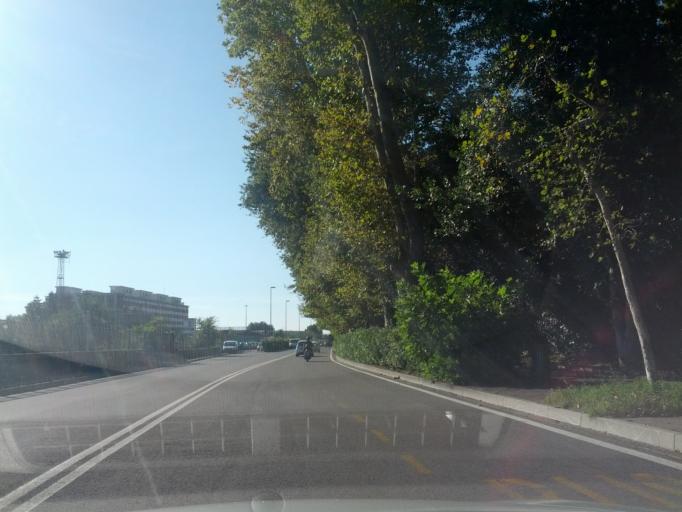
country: IT
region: Friuli Venezia Giulia
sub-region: Provincia di Trieste
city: Trieste
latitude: 45.6404
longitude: 13.7563
